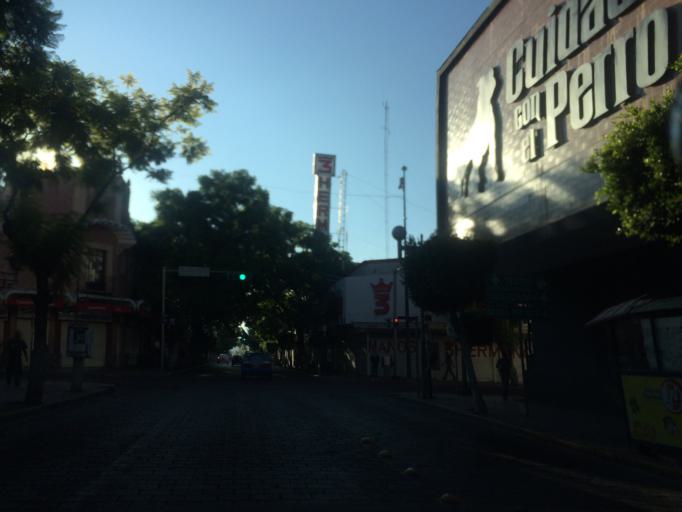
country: MX
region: Puebla
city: Tehuacan
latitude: 18.4630
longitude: -97.3944
